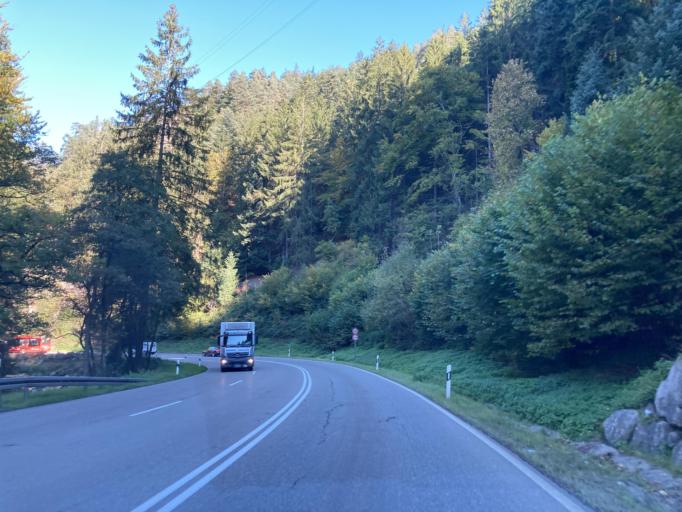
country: DE
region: Baden-Wuerttemberg
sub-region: Freiburg Region
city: Triberg im Schwarzwald
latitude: 48.1669
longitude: 8.2358
